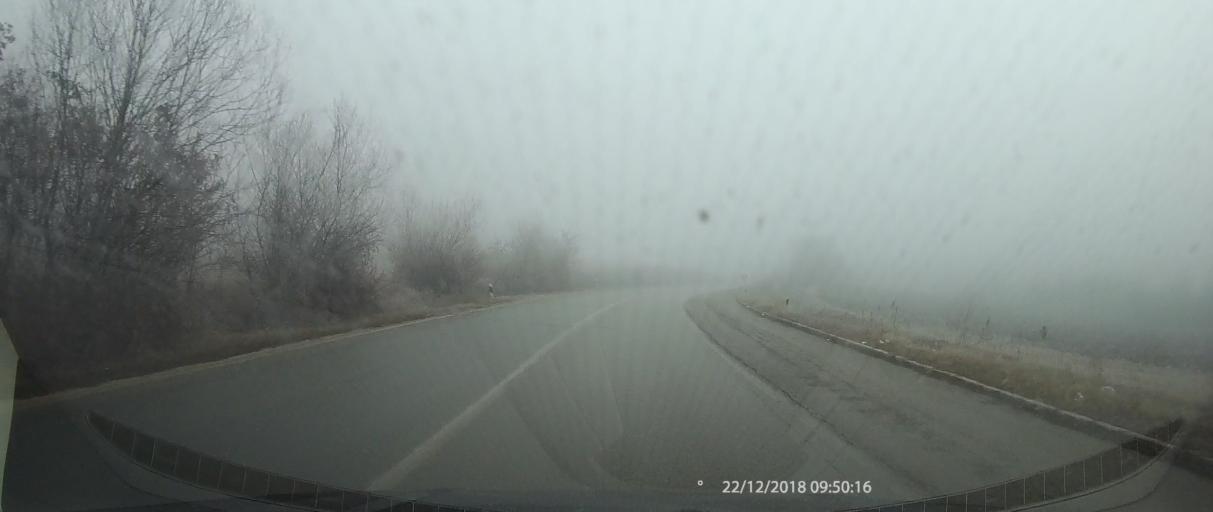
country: MK
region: Staro Nagoricane
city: Staro Nagorichane
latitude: 42.1749
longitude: 21.7853
